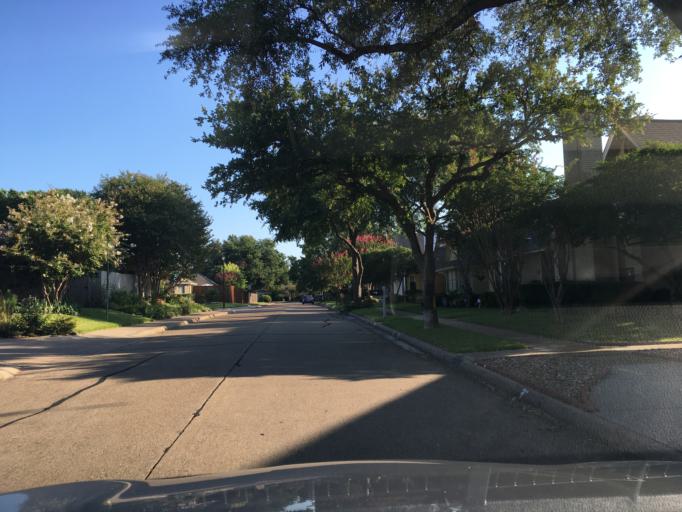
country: US
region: Texas
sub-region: Dallas County
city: Addison
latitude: 32.9678
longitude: -96.8559
